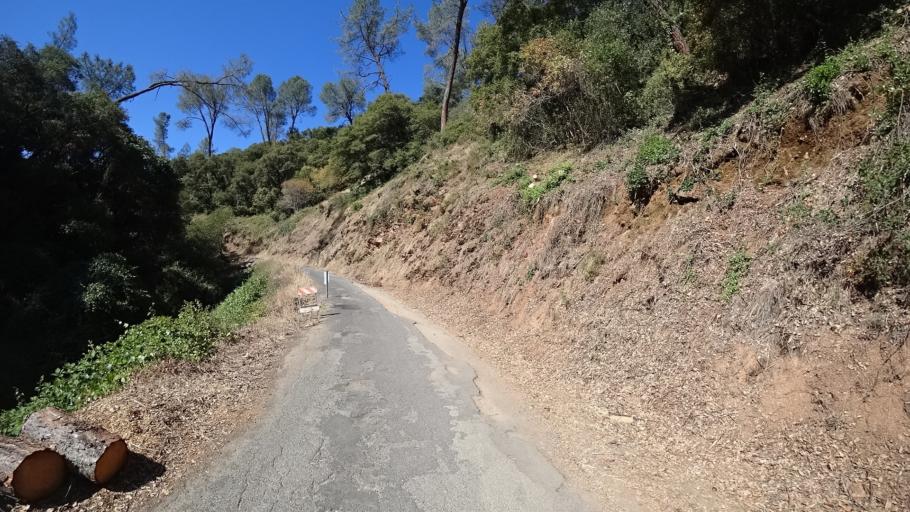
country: US
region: California
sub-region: Amador County
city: Jackson
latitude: 38.2708
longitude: -120.7606
